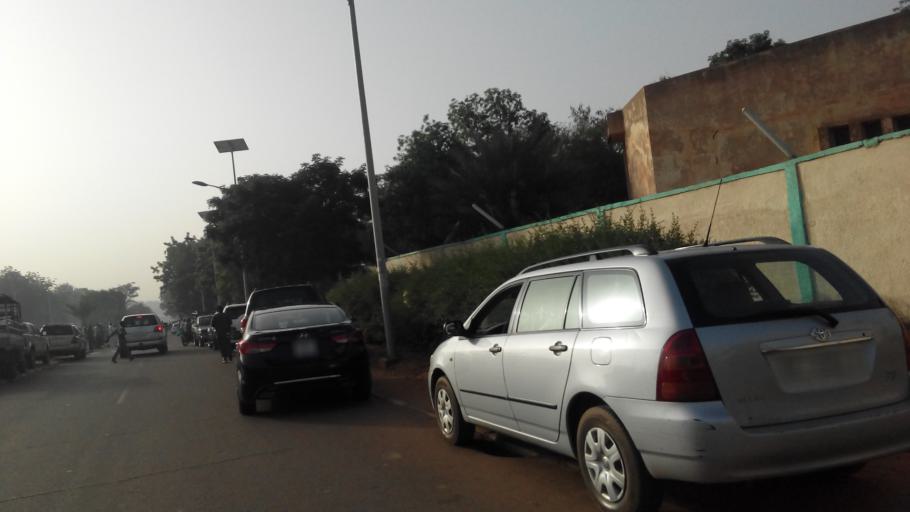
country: NE
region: Niamey
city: Niamey
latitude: 13.5146
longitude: 2.1017
